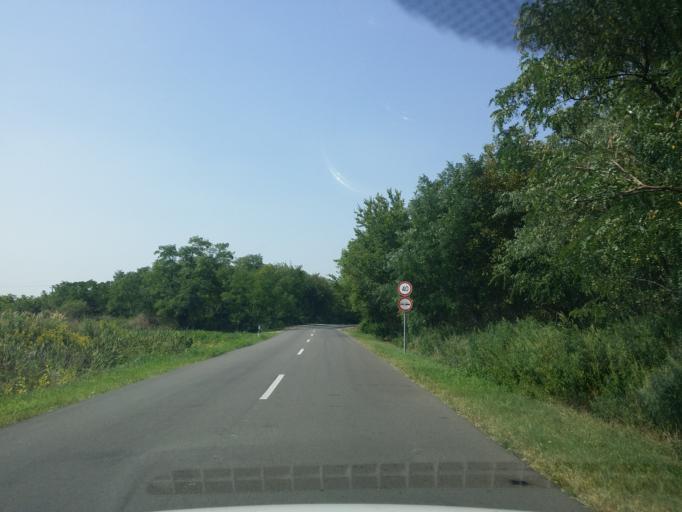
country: HU
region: Tolna
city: Pincehely
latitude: 46.6173
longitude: 18.4196
